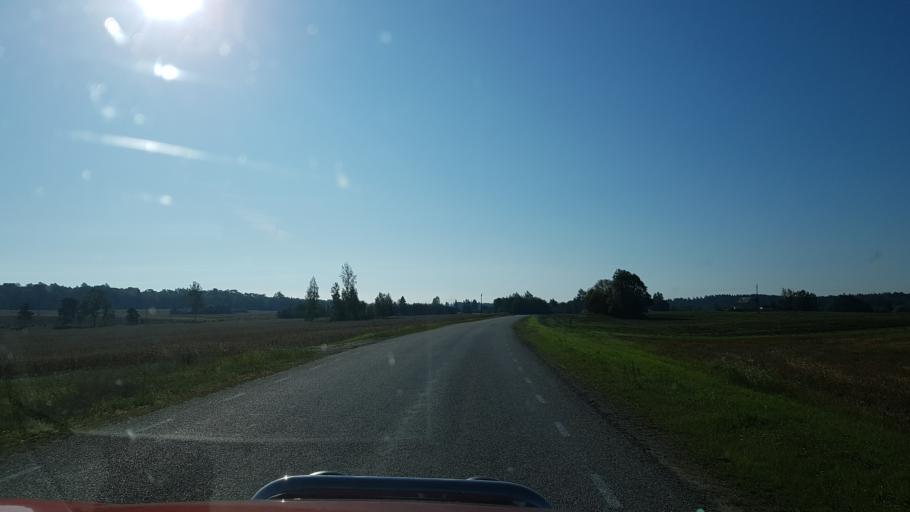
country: EE
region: Jogevamaa
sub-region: Tabivere vald
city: Tabivere
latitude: 58.6752
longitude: 26.7438
